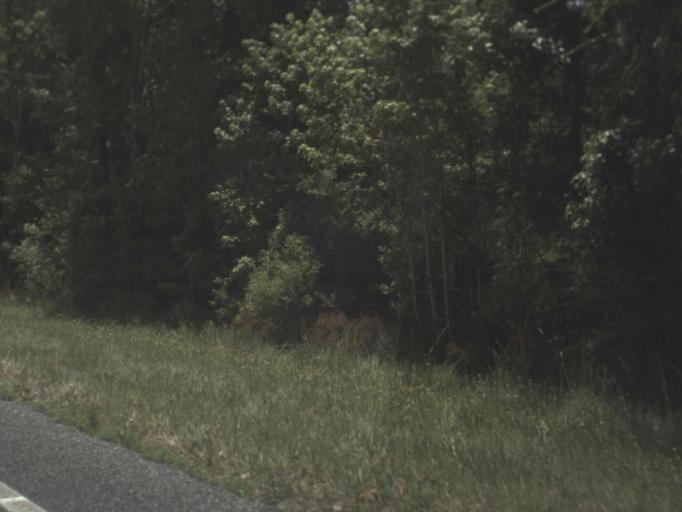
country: US
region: Florida
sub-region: Taylor County
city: Steinhatchee
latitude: 29.8738
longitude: -83.4018
